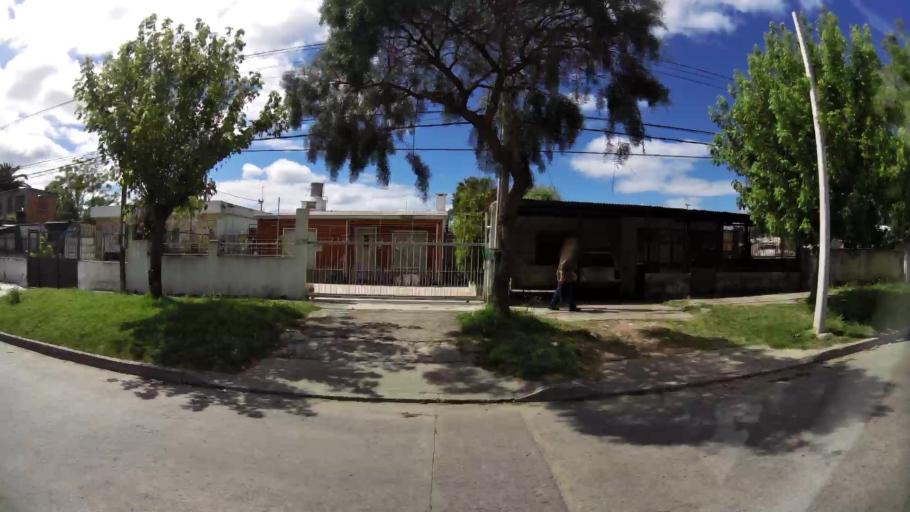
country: UY
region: Canelones
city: Paso de Carrasco
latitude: -34.8645
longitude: -56.1201
